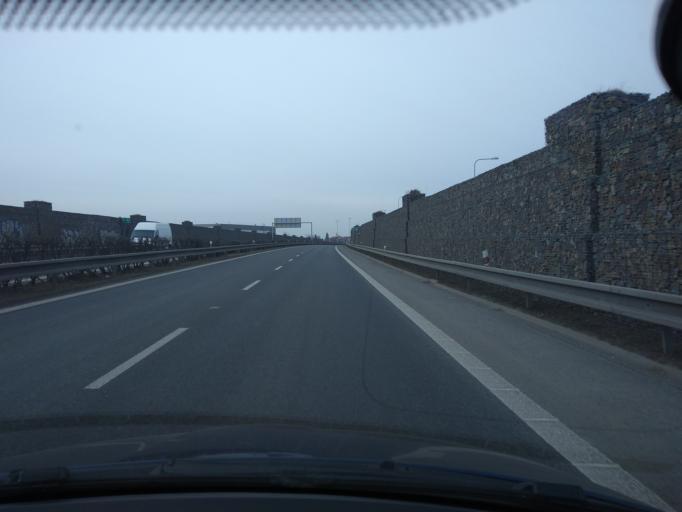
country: CZ
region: Plzensky
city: Stary Plzenec
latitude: 49.7067
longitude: 13.4294
